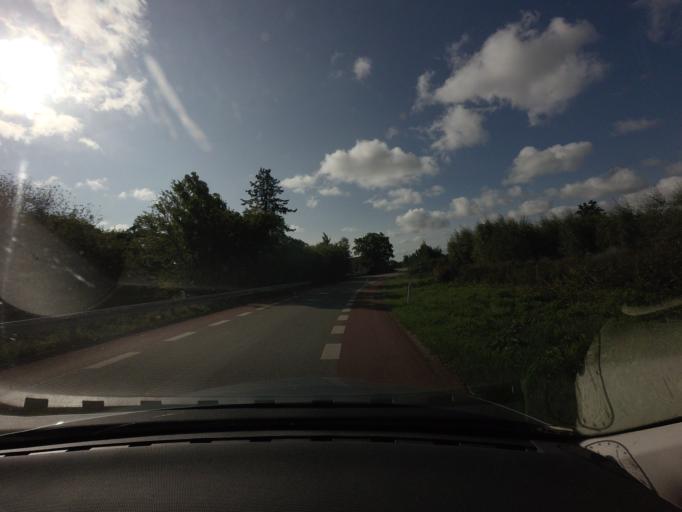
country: DK
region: Zealand
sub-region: Vordingborg Kommune
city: Praesto
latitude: 55.1370
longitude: 12.0180
